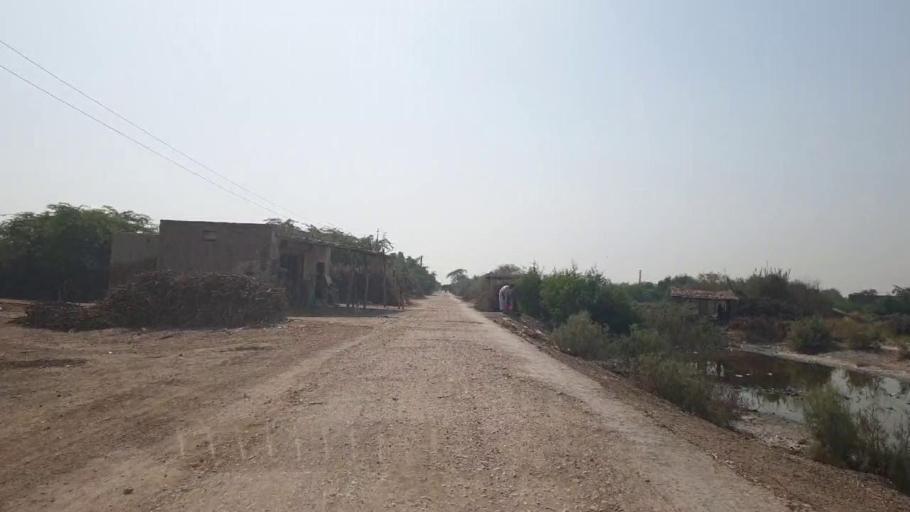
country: PK
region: Sindh
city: Berani
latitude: 25.8932
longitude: 68.7505
